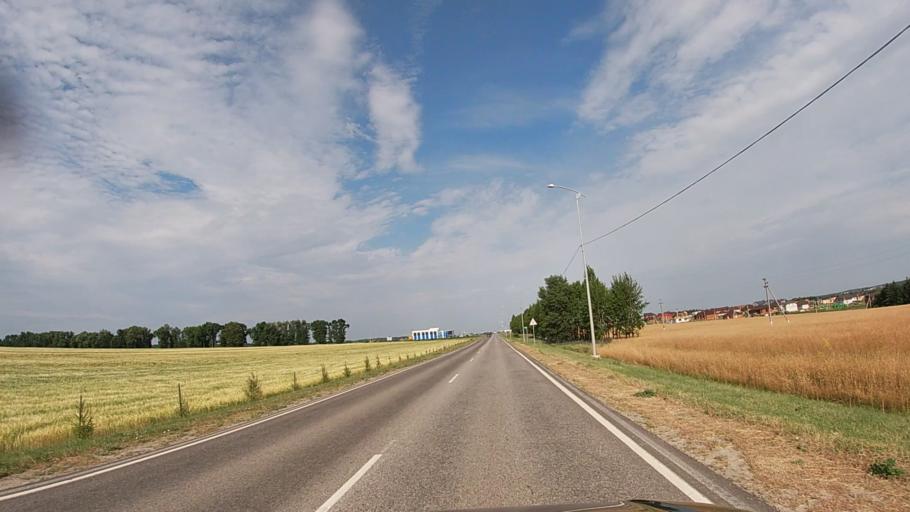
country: RU
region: Belgorod
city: Krasnaya Yaruga
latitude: 50.7960
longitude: 35.7004
